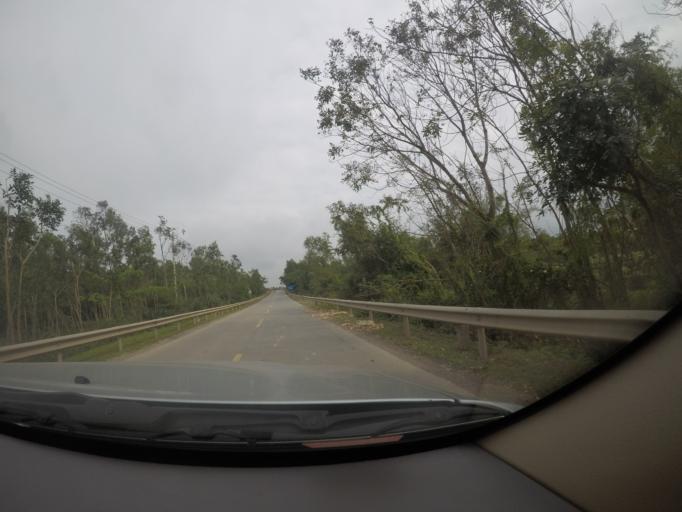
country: VN
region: Quang Binh
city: Kwang Binh
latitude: 17.4266
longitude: 106.5907
